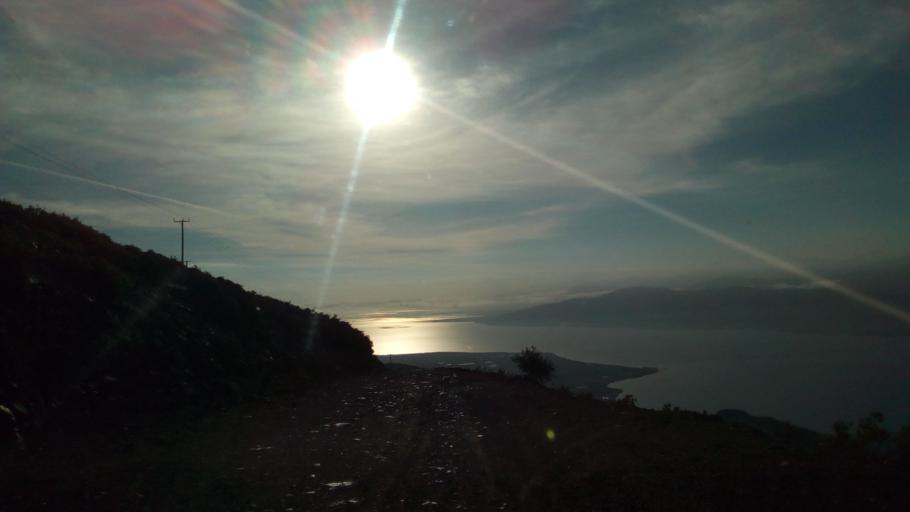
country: GR
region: West Greece
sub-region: Nomos Aitolias kai Akarnanias
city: Nafpaktos
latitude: 38.4201
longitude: 21.8035
